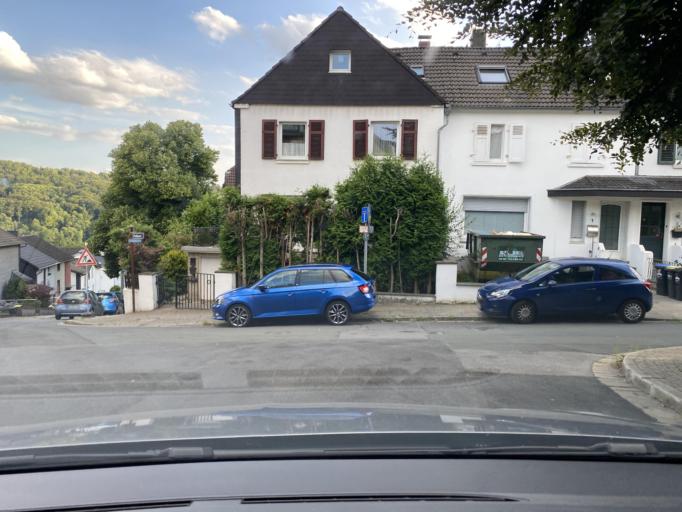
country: DE
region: North Rhine-Westphalia
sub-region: Regierungsbezirk Dusseldorf
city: Heiligenhaus
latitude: 51.3655
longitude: 6.9505
